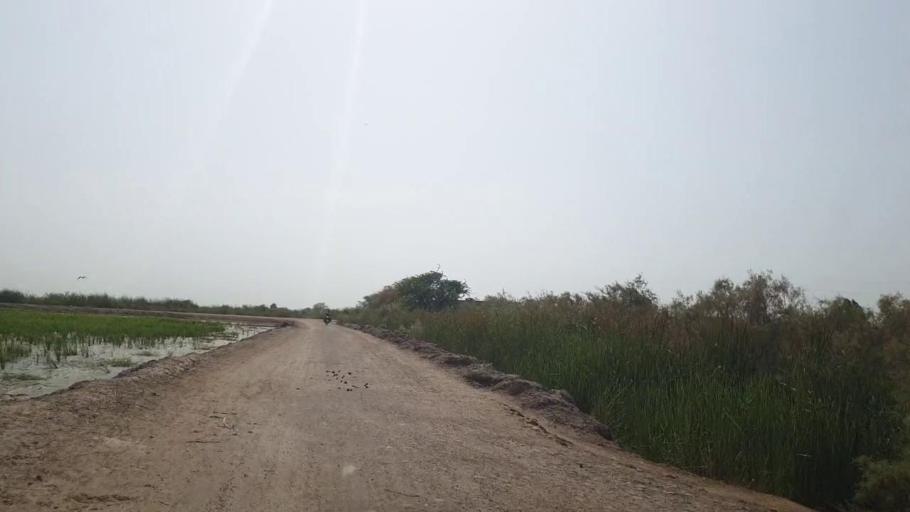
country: PK
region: Sindh
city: Daur
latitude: 26.3194
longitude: 68.2221
